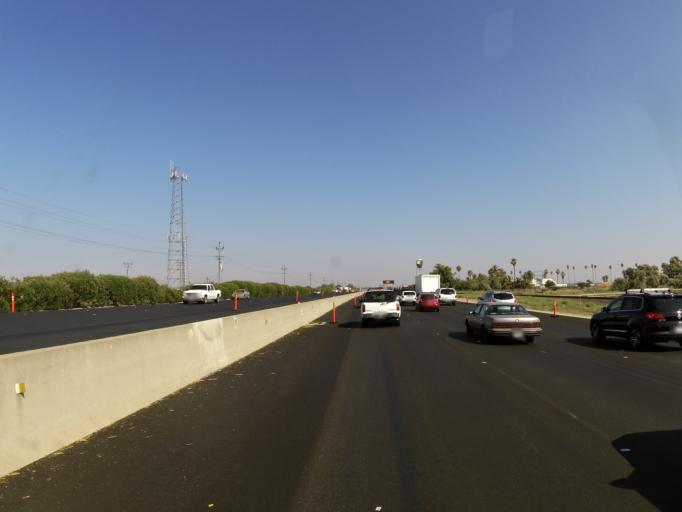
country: US
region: California
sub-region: San Joaquin County
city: Manteca
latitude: 37.7687
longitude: -121.1709
